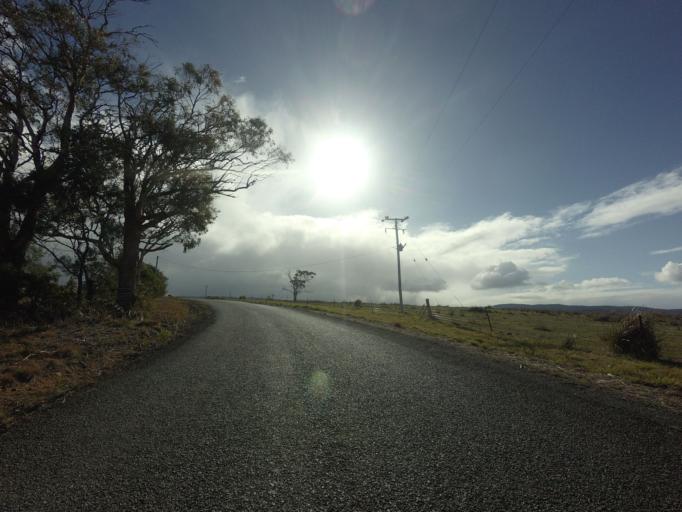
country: AU
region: Tasmania
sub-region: Sorell
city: Sorell
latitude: -42.3019
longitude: 147.9928
